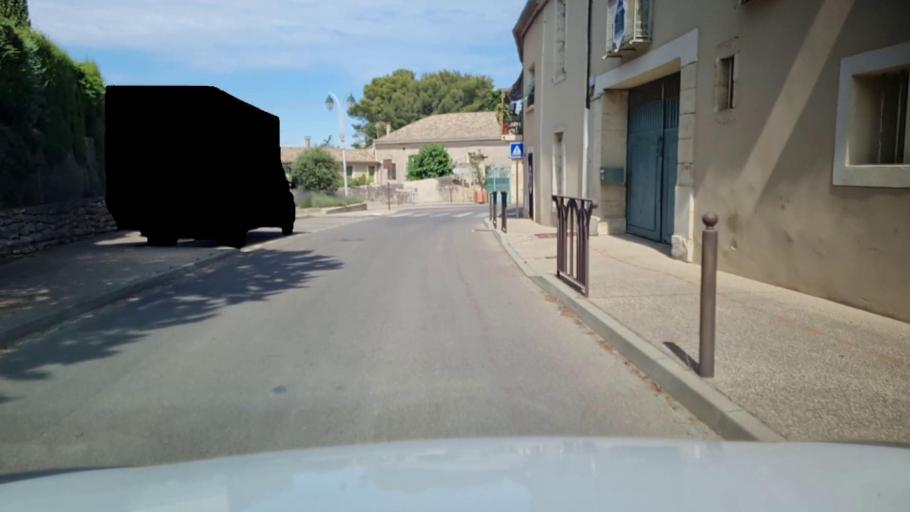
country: FR
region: Languedoc-Roussillon
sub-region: Departement du Gard
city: Nages-et-Solorgues
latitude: 43.7895
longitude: 4.2318
